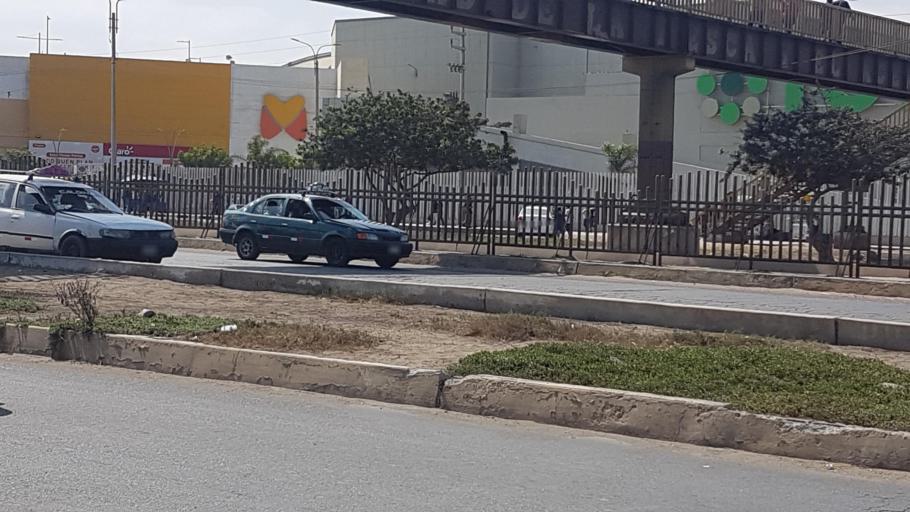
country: PE
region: Ancash
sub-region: Provincia de Santa
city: Chimbote
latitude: -9.1044
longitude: -78.5578
